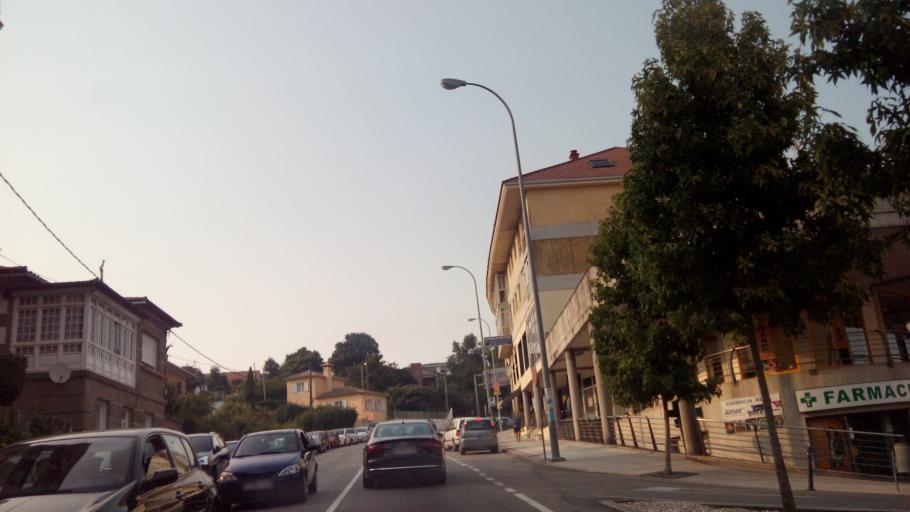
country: ES
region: Galicia
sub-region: Provincia de Pontevedra
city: Nigran
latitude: 42.1176
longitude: -8.8130
